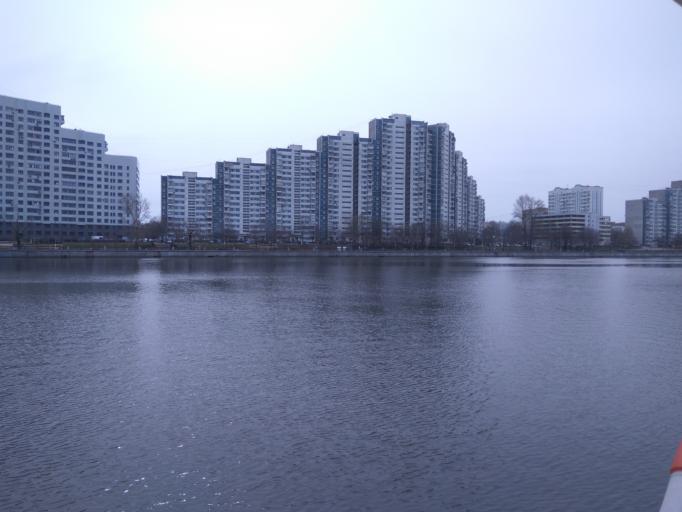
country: RU
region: Moskovskaya
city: Kozhukhovo
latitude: 55.6916
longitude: 37.6846
